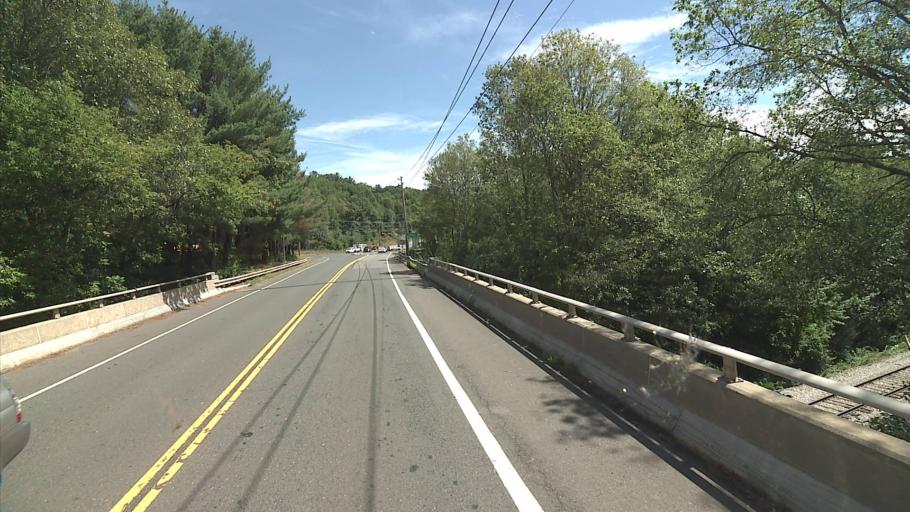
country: US
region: Connecticut
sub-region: Tolland County
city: Storrs
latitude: 41.8353
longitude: -72.3082
